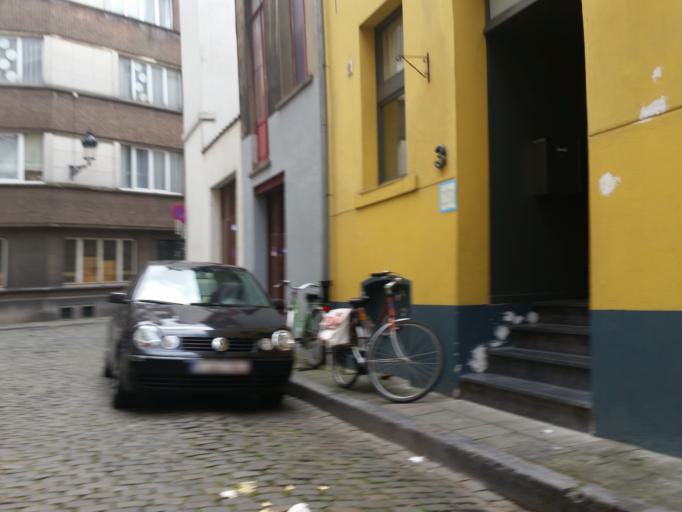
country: BE
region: Brussels Capital
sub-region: Bruxelles-Capitale
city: Brussels
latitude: 50.8538
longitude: 4.3476
